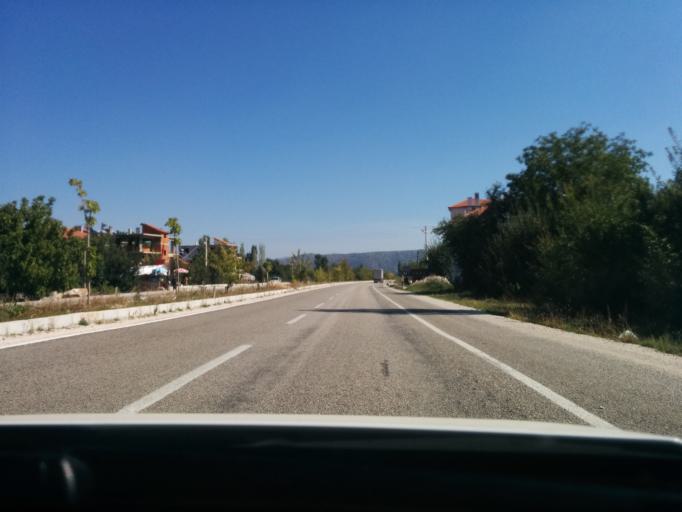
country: TR
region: Antalya
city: Korkuteli
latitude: 37.0511
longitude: 30.1981
